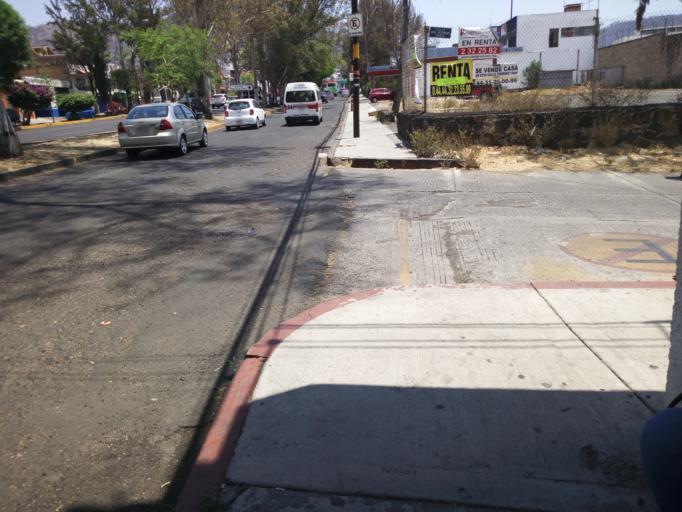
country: MX
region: Michoacan
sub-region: Morelia
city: Puerto de Buenavista (Lazaro Cardenas)
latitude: 19.6942
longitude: -101.1530
